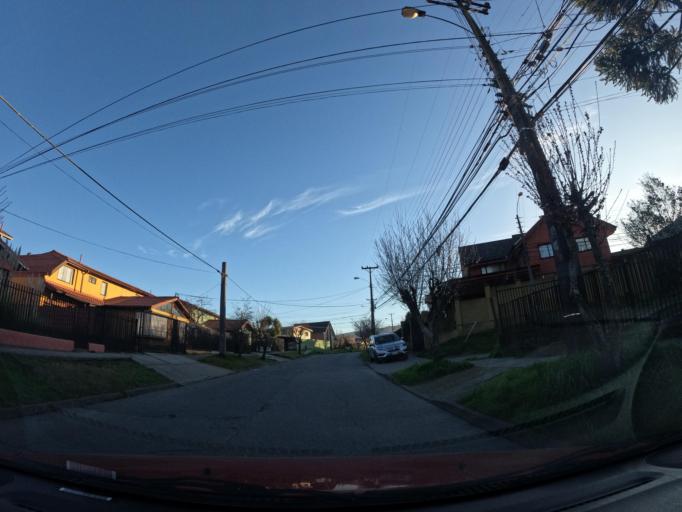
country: CL
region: Biobio
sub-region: Provincia de Concepcion
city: Chiguayante
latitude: -36.9205
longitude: -73.0287
